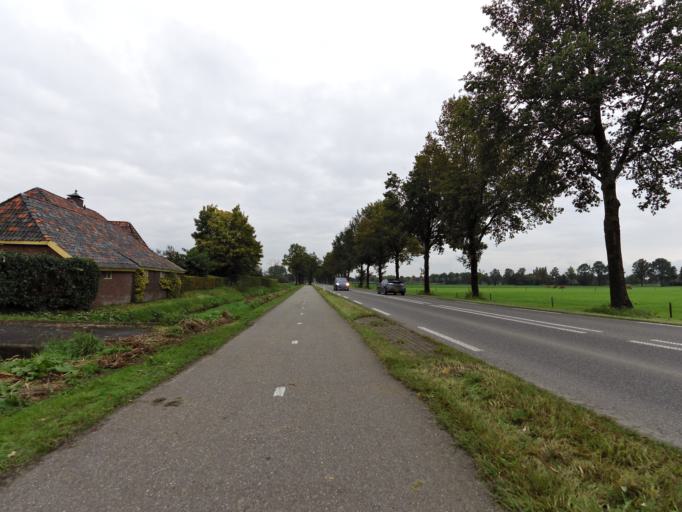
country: NL
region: Gelderland
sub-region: Oude IJsselstreek
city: Gendringen
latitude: 51.8952
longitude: 6.3598
